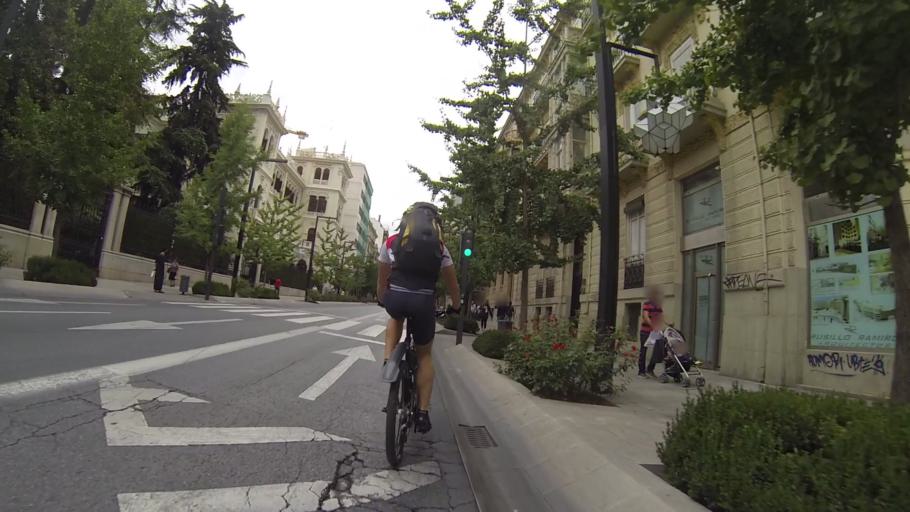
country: ES
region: Andalusia
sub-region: Provincia de Granada
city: Granada
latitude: 37.1818
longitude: -3.6007
